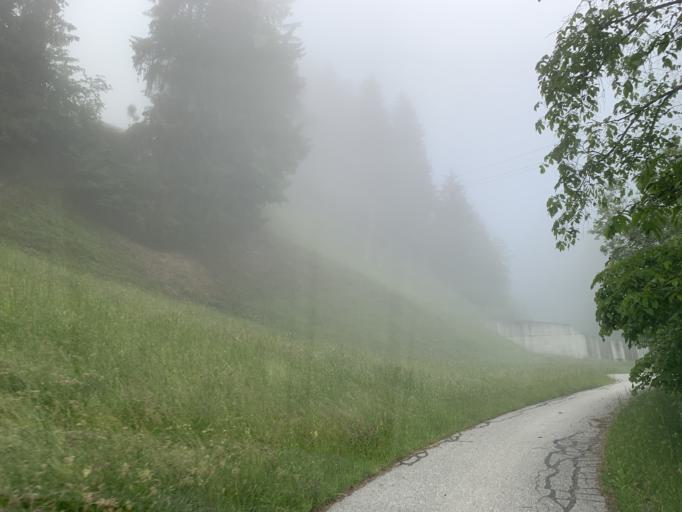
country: AT
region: Styria
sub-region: Politischer Bezirk Liezen
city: Schladming
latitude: 47.3931
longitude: 13.6194
